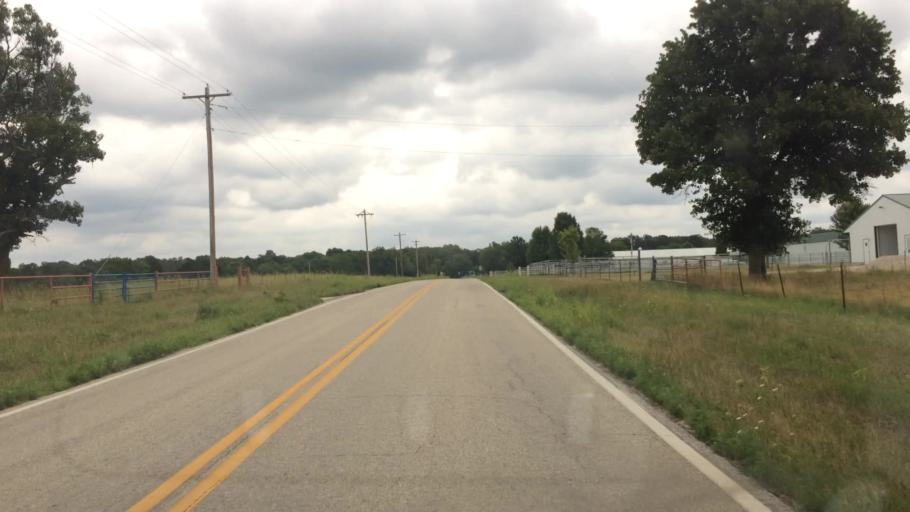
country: US
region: Missouri
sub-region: Greene County
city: Strafford
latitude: 37.2960
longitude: -93.1180
